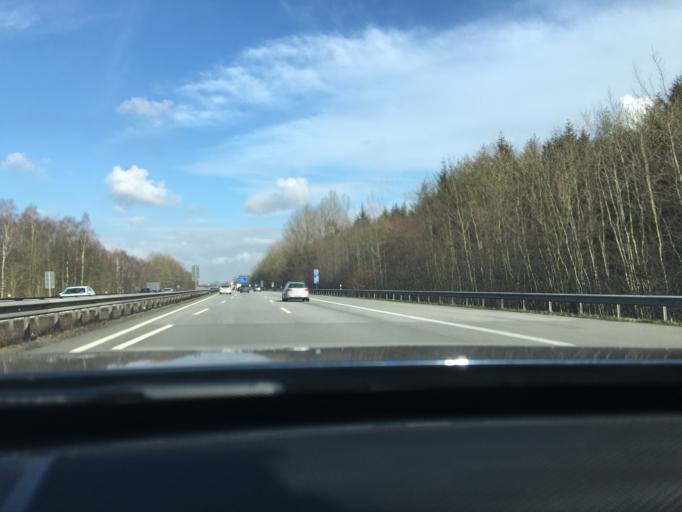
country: DE
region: Lower Saxony
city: Dinklage
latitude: 52.6499
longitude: 8.1584
